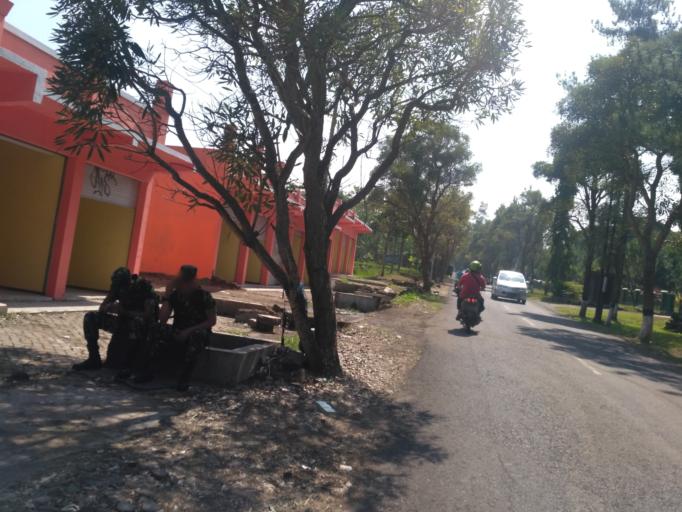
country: ID
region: East Java
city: Batu
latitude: -7.8991
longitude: 112.5816
